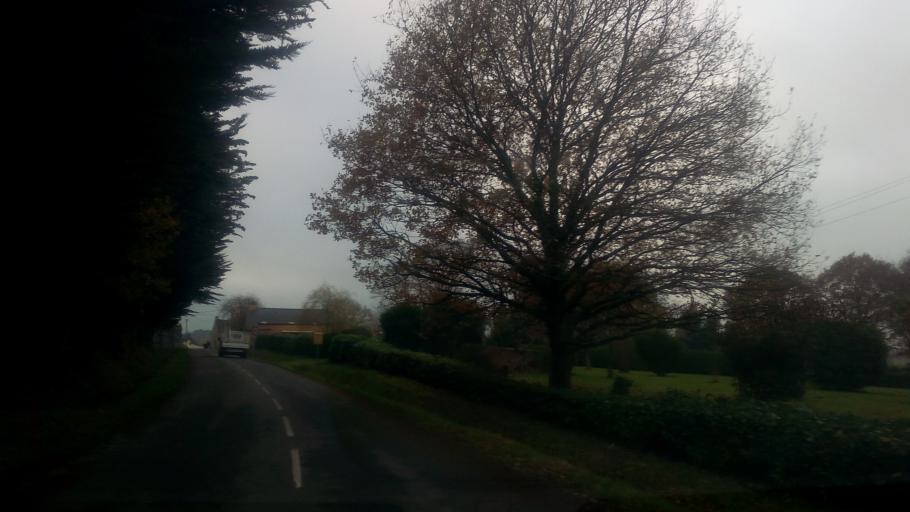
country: FR
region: Brittany
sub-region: Departement du Morbihan
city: Saint-Perreux
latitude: 47.6603
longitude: -2.1202
